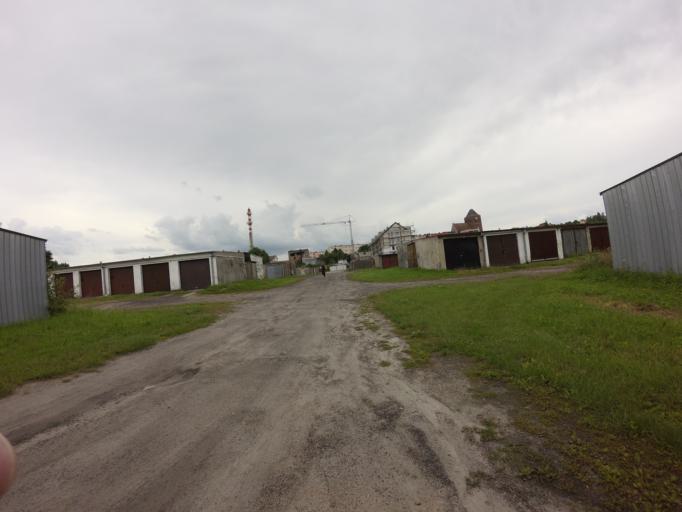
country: PL
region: West Pomeranian Voivodeship
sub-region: Powiat choszczenski
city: Choszczno
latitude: 53.1712
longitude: 15.4212
